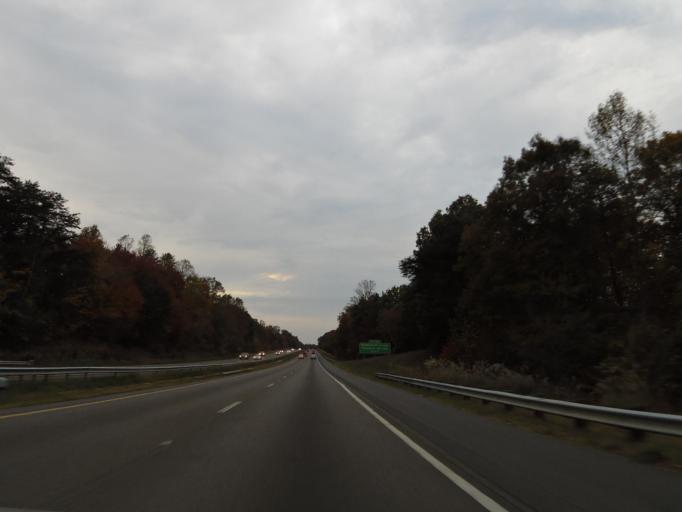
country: US
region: North Carolina
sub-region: Burke County
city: Icard
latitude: 35.7279
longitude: -81.4937
